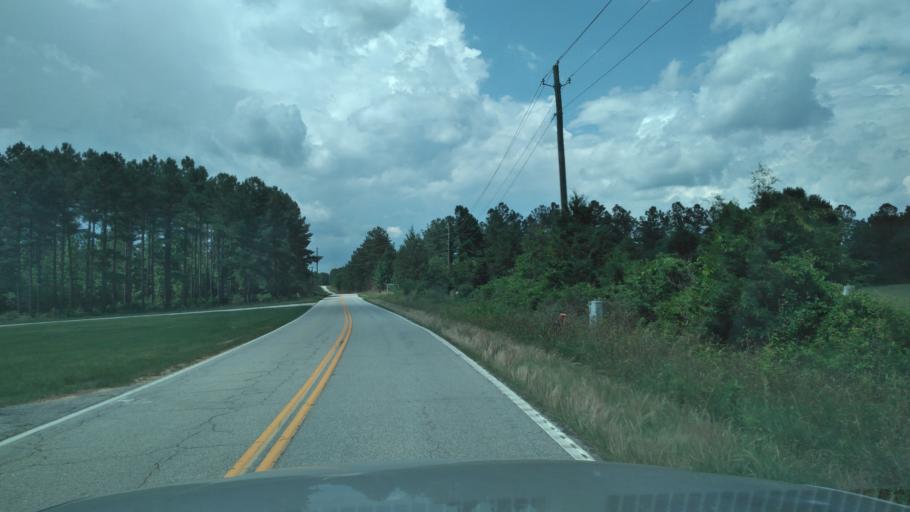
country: US
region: South Carolina
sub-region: Laurens County
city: Laurens
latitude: 34.5180
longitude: -82.0933
